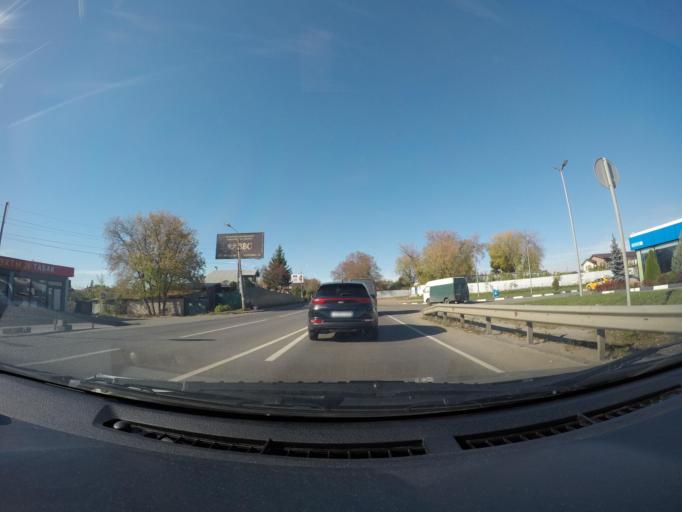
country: RU
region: Moskovskaya
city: Kraskovo
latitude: 55.6315
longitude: 37.9772
